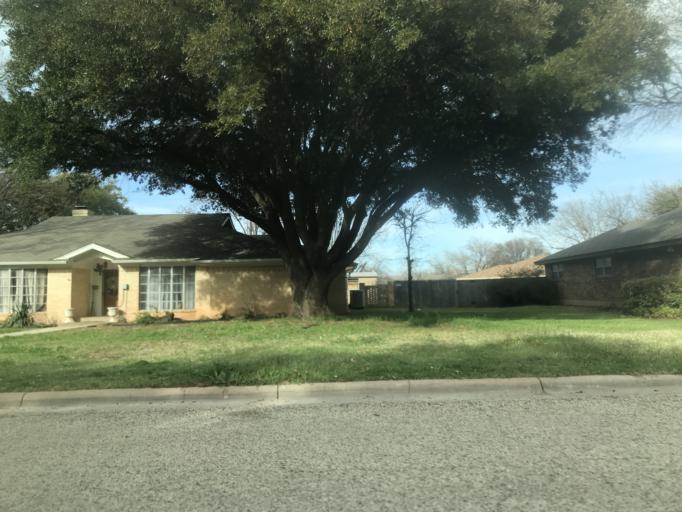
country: US
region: Texas
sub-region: Taylor County
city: Abilene
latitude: 32.4146
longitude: -99.7723
